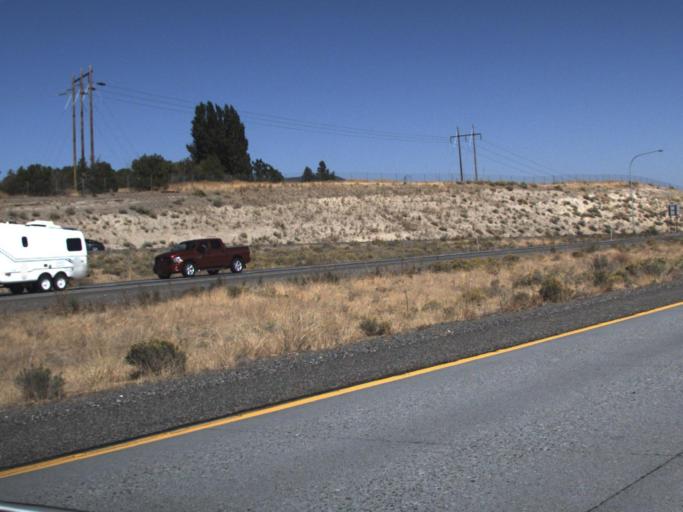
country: US
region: Washington
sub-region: Benton County
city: Richland
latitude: 46.2552
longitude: -119.3015
